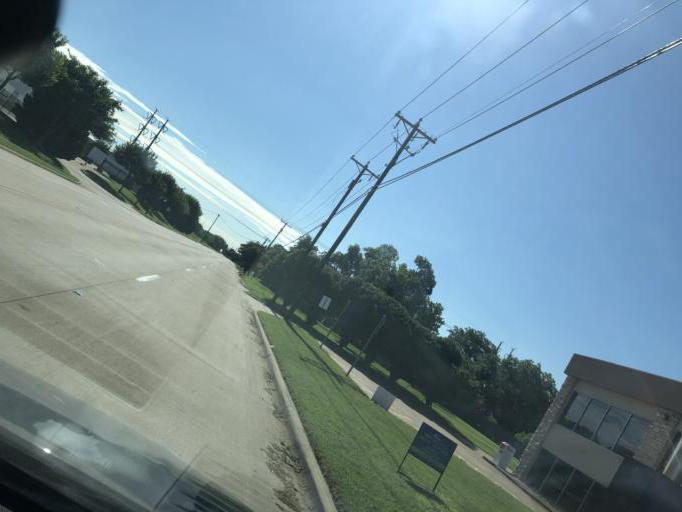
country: US
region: Texas
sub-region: Tarrant County
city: Euless
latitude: 32.8033
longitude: -97.0288
